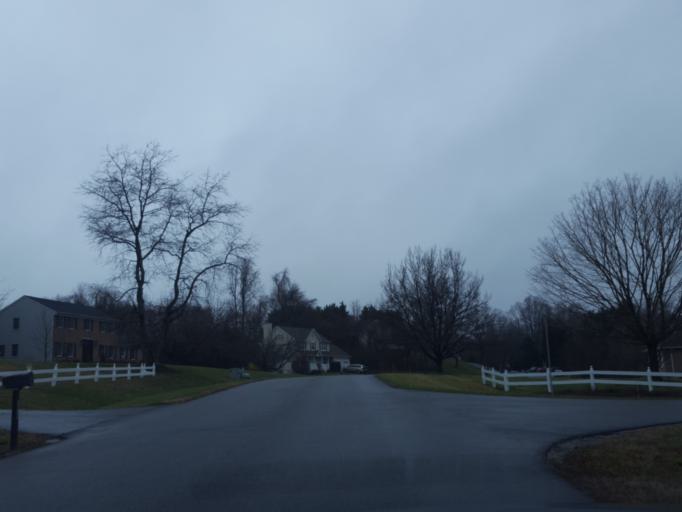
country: US
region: Maryland
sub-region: Calvert County
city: Chesapeake Beach
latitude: 38.6130
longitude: -76.5385
